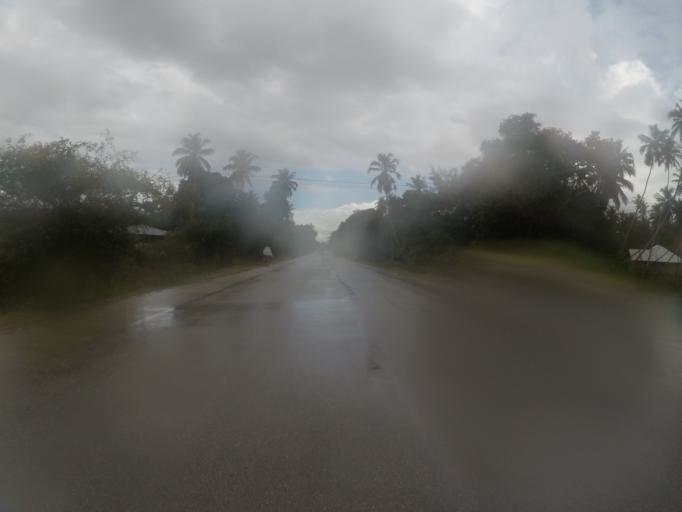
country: TZ
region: Zanzibar Central/South
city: Koani
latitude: -6.0246
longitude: 39.2106
